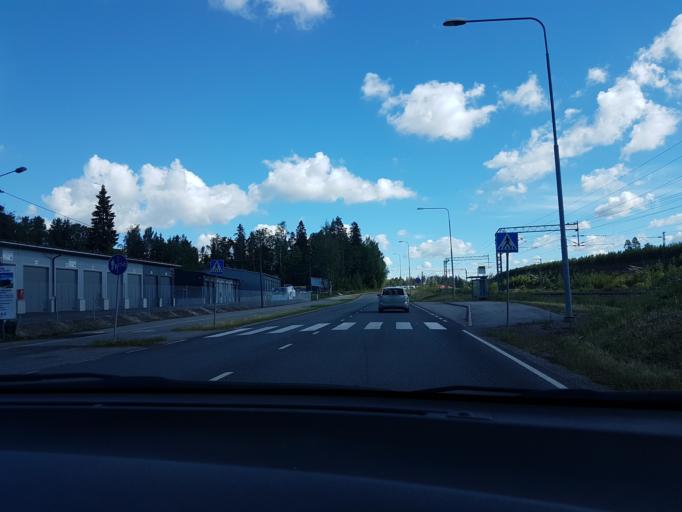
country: FI
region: Uusimaa
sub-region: Helsinki
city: Kerava
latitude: 60.3714
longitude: 25.0933
